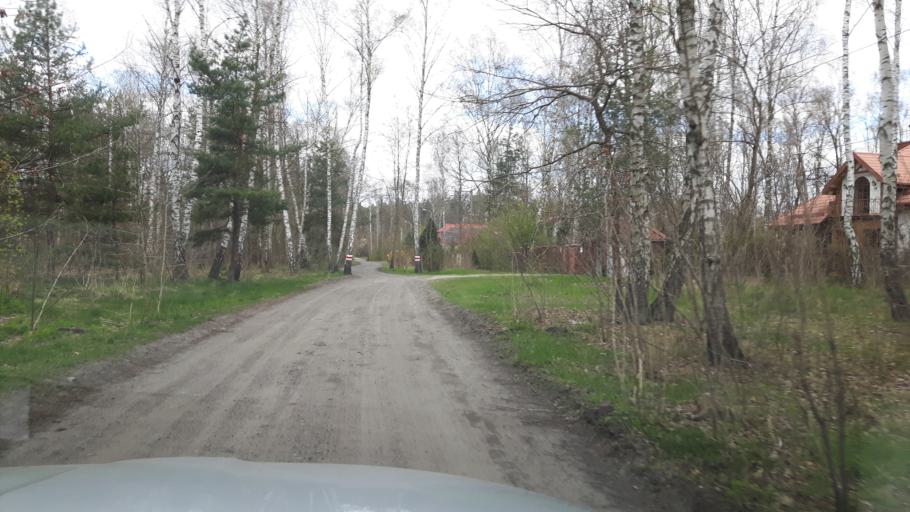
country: PL
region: Masovian Voivodeship
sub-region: Powiat wolominski
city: Wolomin
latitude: 52.3490
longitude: 21.2208
